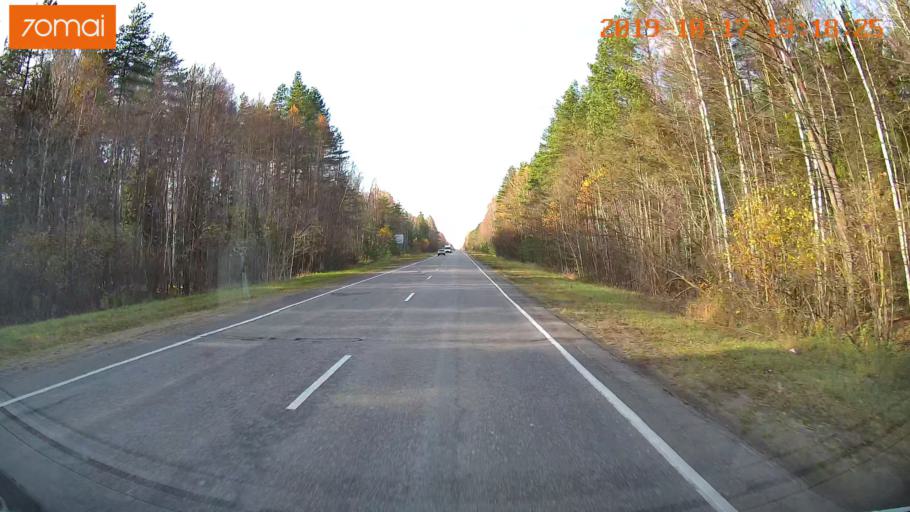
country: RU
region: Rjazan
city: Gus'-Zheleznyy
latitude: 55.0629
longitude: 41.0982
